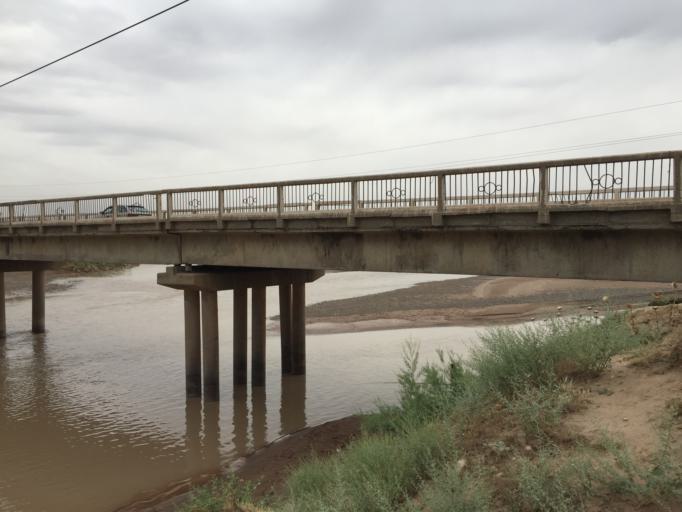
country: TJ
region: Khatlon
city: Vose'
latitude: 37.7856
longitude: 69.5684
